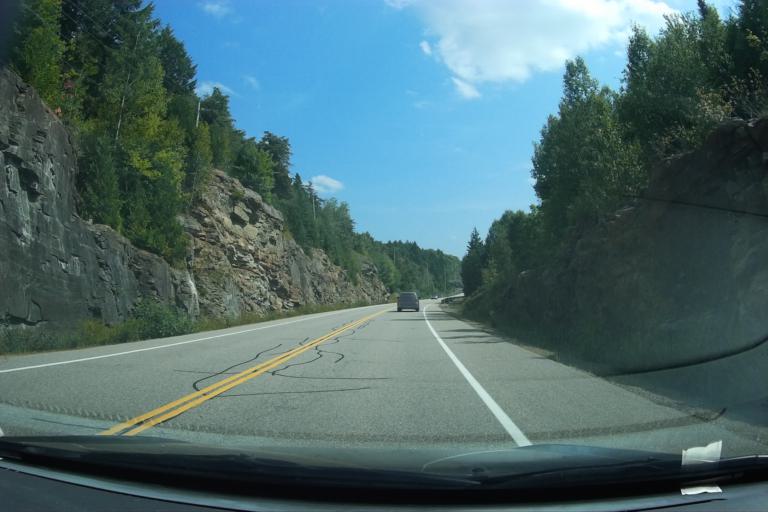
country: CA
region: Ontario
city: Mattawa
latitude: 45.5828
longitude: -78.4694
